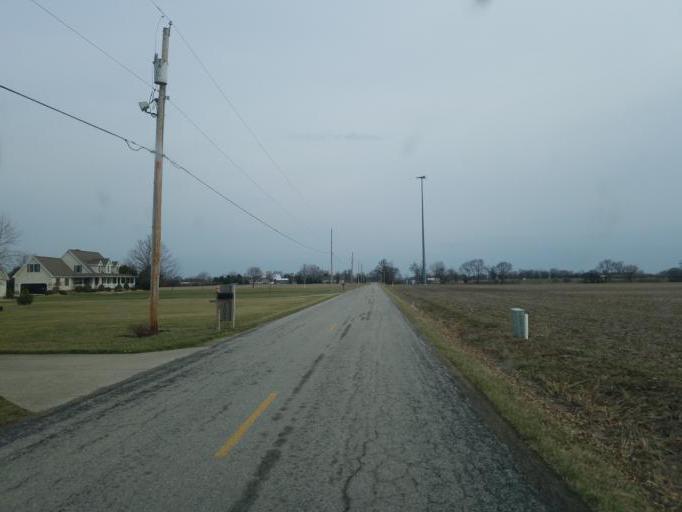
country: US
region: Ohio
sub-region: Marion County
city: Marion
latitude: 40.6188
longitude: -83.0051
